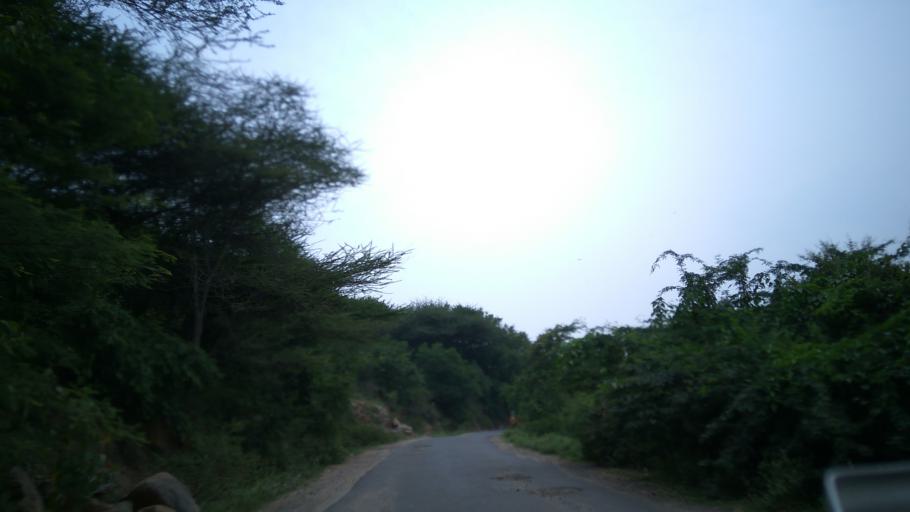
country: IN
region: Tamil Nadu
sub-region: Dharmapuri
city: Dharmapuri
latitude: 12.0145
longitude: 78.1282
